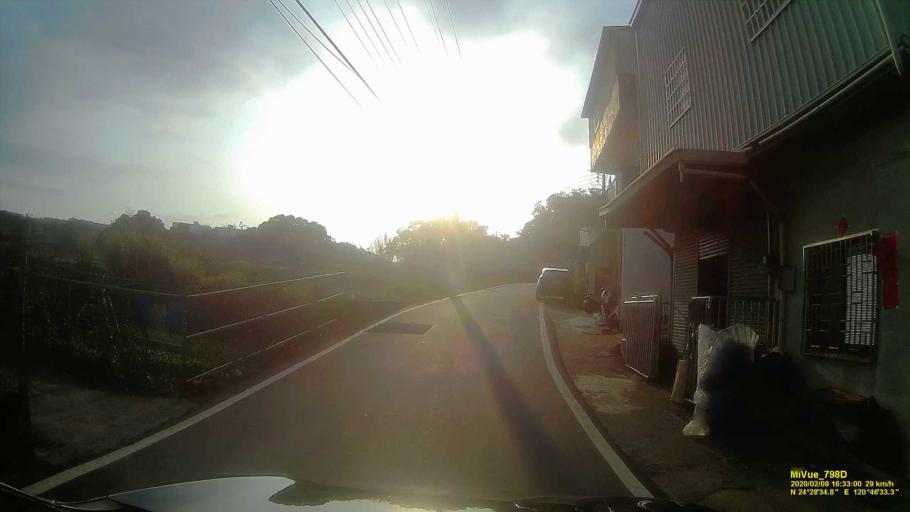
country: TW
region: Taiwan
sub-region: Miaoli
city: Miaoli
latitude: 24.4763
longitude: 120.7757
